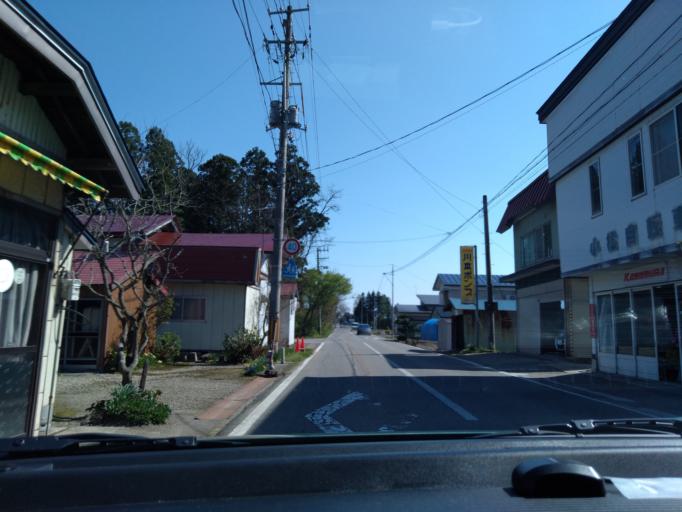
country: JP
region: Akita
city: Kakunodatemachi
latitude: 39.5394
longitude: 140.5852
